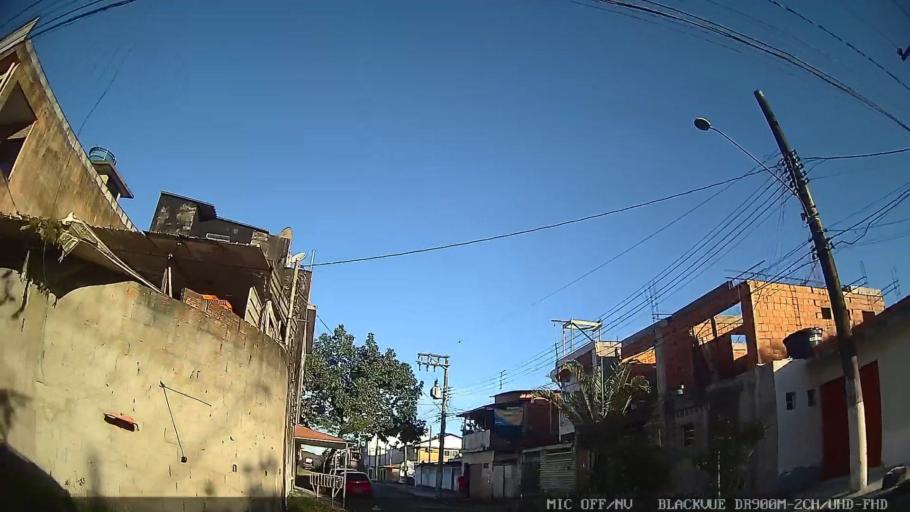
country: BR
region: Sao Paulo
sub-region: Guaruja
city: Guaruja
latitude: -23.9602
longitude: -46.2764
